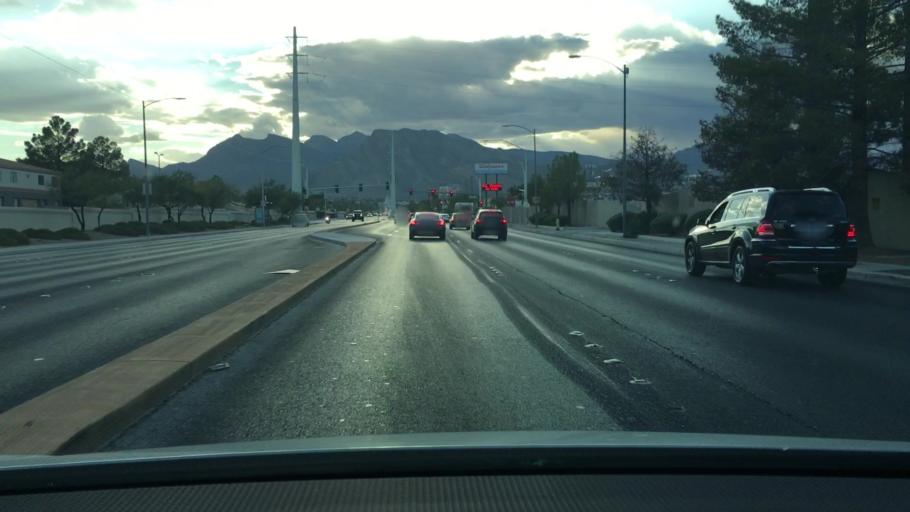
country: US
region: Nevada
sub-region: Clark County
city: Summerlin South
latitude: 36.2186
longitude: -115.2769
